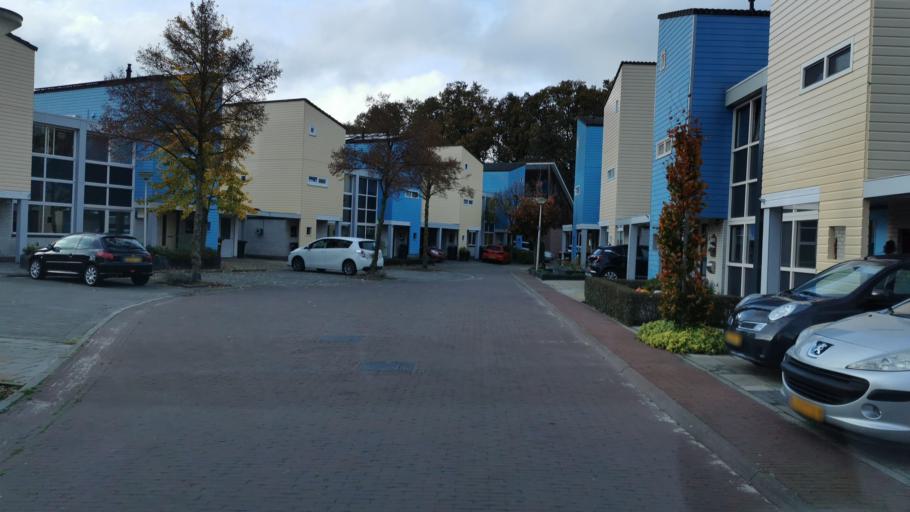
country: DE
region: North Rhine-Westphalia
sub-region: Regierungsbezirk Munster
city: Gronau
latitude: 52.2053
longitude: 6.9693
